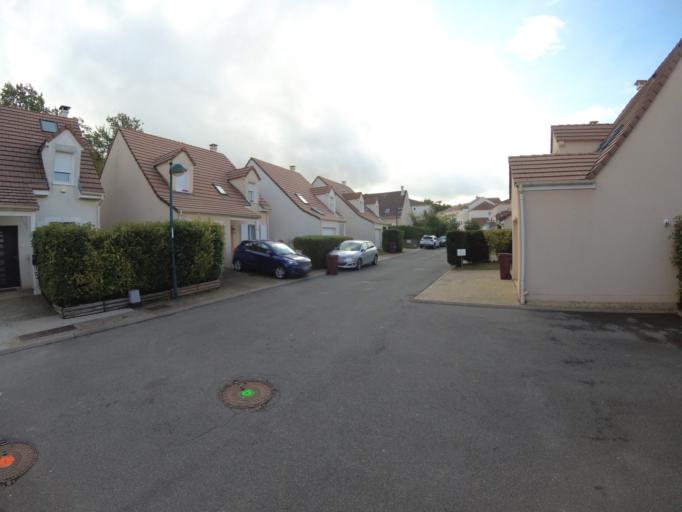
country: FR
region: Ile-de-France
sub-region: Departement de Seine-et-Marne
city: Montevrain
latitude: 48.8703
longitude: 2.7531
